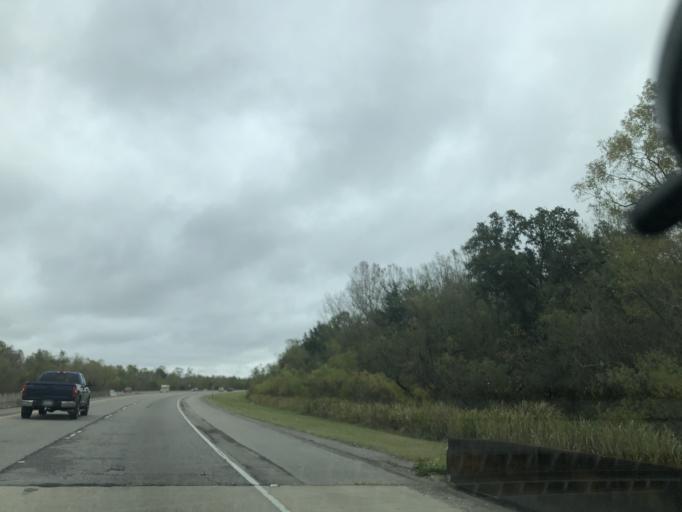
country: US
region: Louisiana
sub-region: Saint Charles Parish
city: Destrehan
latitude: 29.9599
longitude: -90.3634
